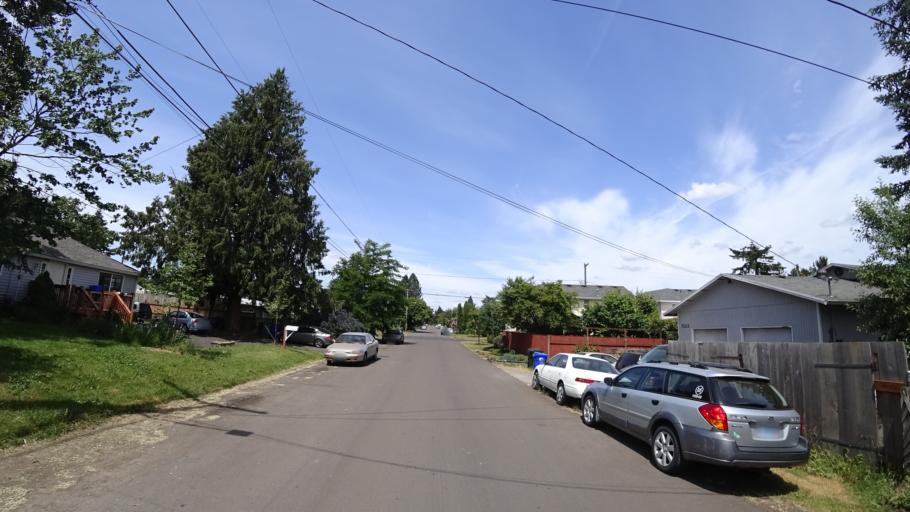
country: US
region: Oregon
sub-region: Multnomah County
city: Lents
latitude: 45.4705
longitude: -122.5952
